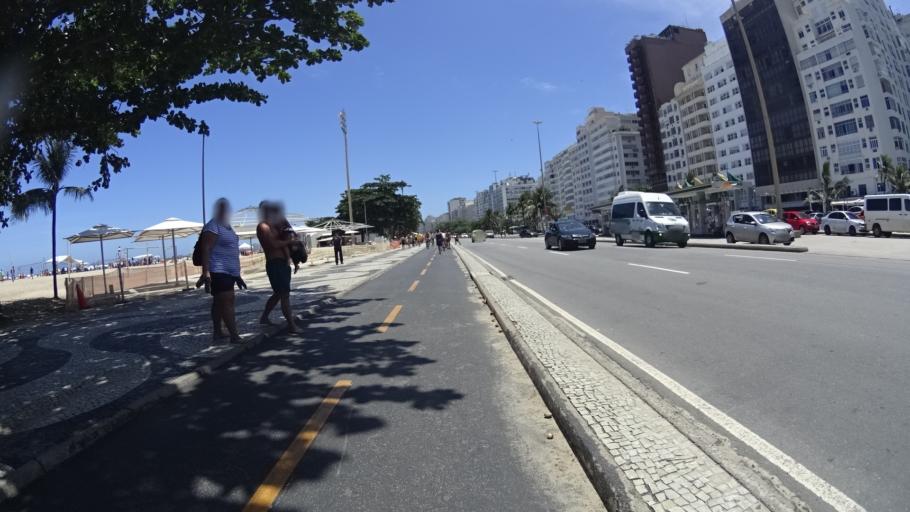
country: BR
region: Rio de Janeiro
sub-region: Rio De Janeiro
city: Rio de Janeiro
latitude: -22.9665
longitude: -43.1759
